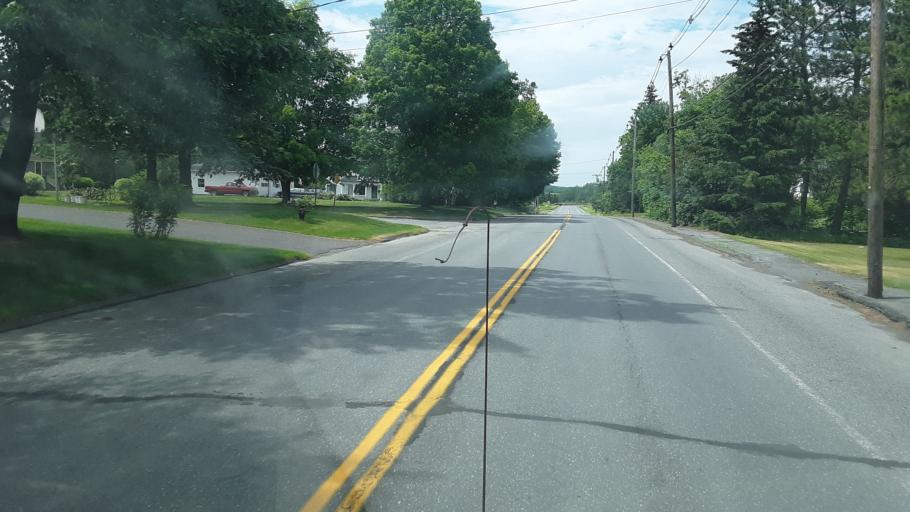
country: US
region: Maine
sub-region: Aroostook County
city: Fort Fairfield
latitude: 46.7743
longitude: -67.8386
